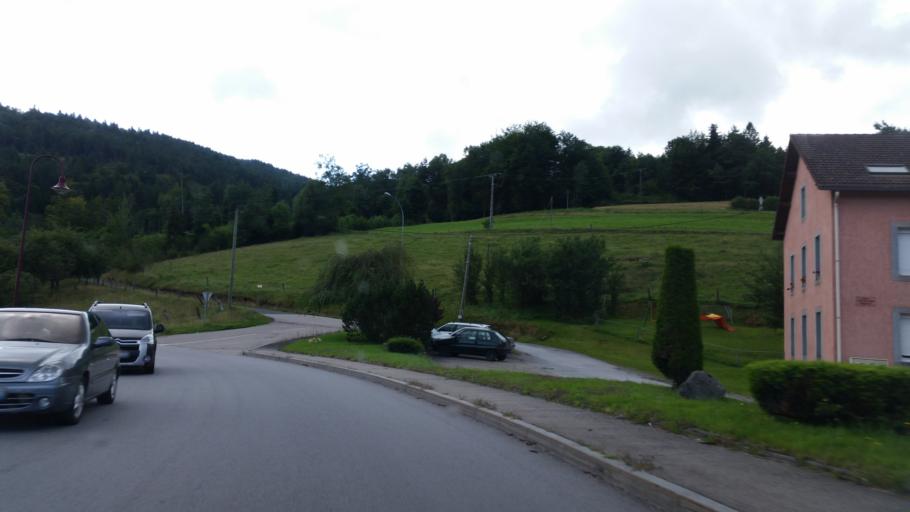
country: FR
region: Lorraine
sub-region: Departement des Vosges
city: Le Tholy
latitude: 48.0578
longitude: 6.7120
